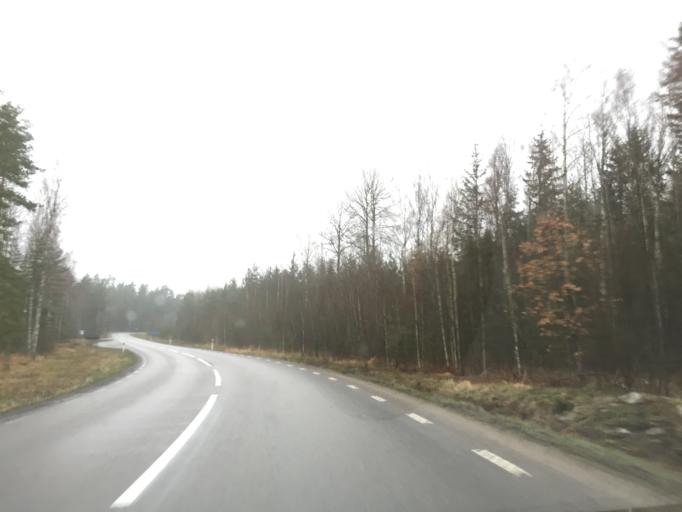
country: SE
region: OErebro
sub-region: Hallsbergs Kommun
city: Skollersta
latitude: 59.2299
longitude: 15.4120
